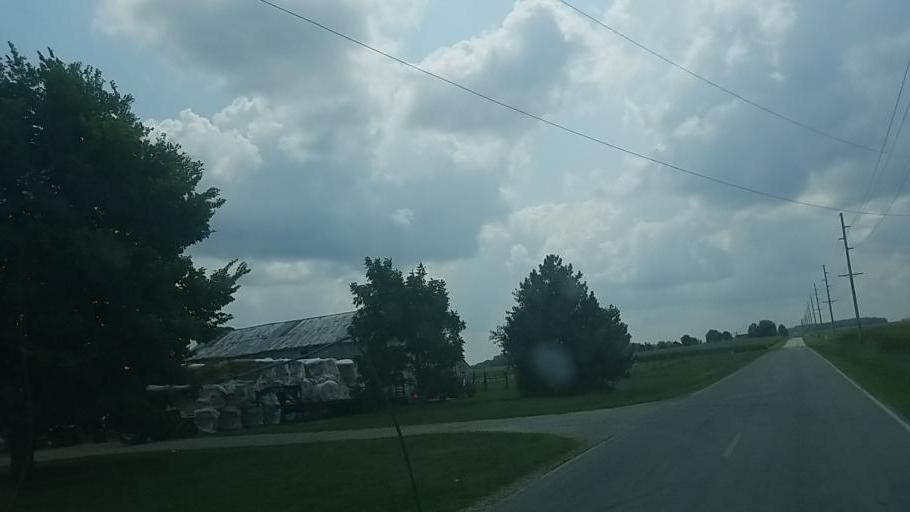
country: US
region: Ohio
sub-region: Wyandot County
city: Upper Sandusky
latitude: 40.8708
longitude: -83.3042
